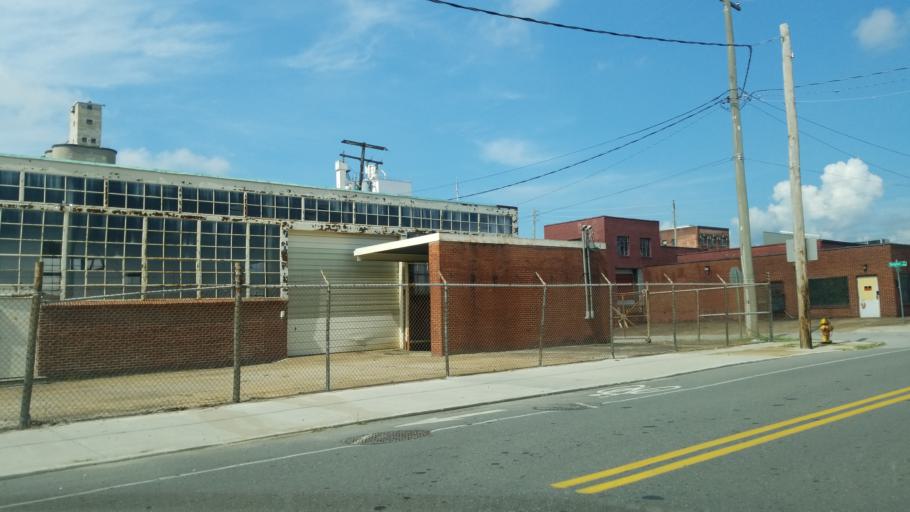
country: US
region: Tennessee
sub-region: Hamilton County
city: Chattanooga
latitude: 35.0427
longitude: -85.3035
